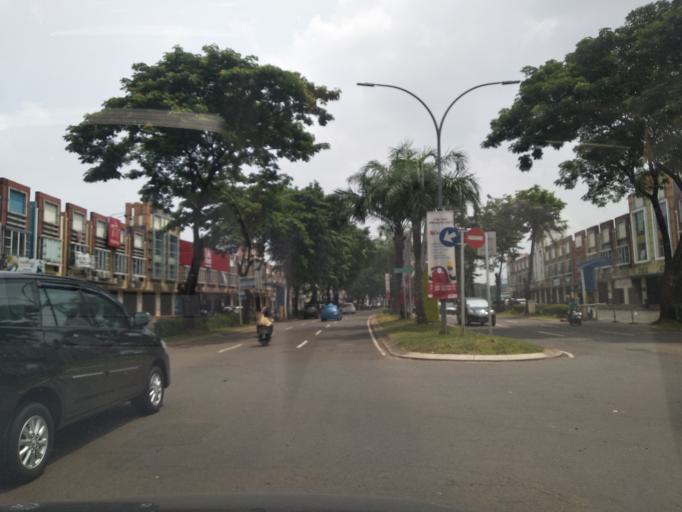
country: ID
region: West Java
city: Bekasi
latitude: -6.2892
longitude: 107.0438
